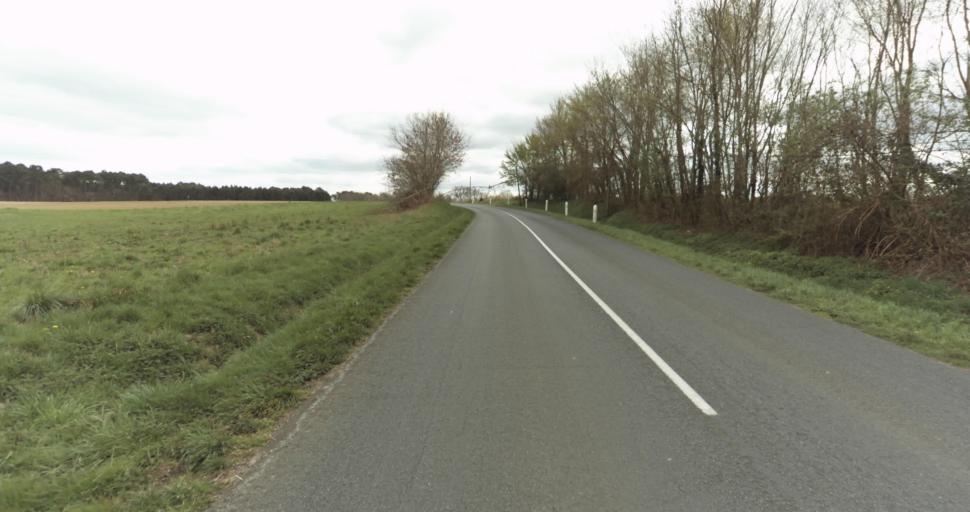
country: FR
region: Aquitaine
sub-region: Departement des Landes
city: Roquefort
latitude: 44.0679
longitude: -0.4217
